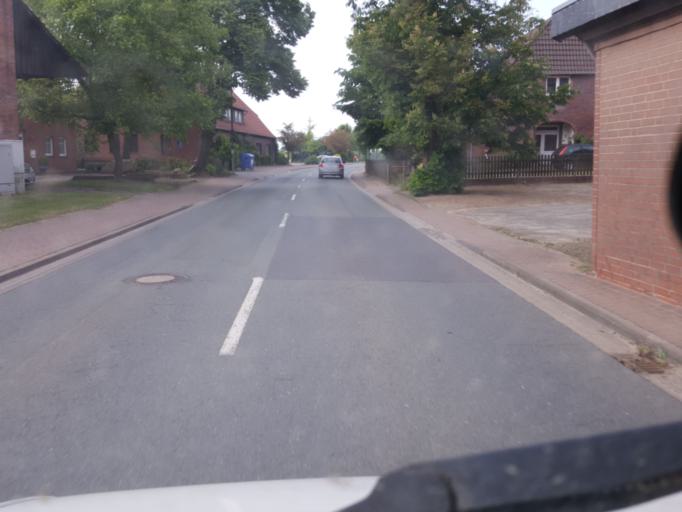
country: DE
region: Lower Saxony
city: Marklohe
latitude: 52.6464
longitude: 9.1470
